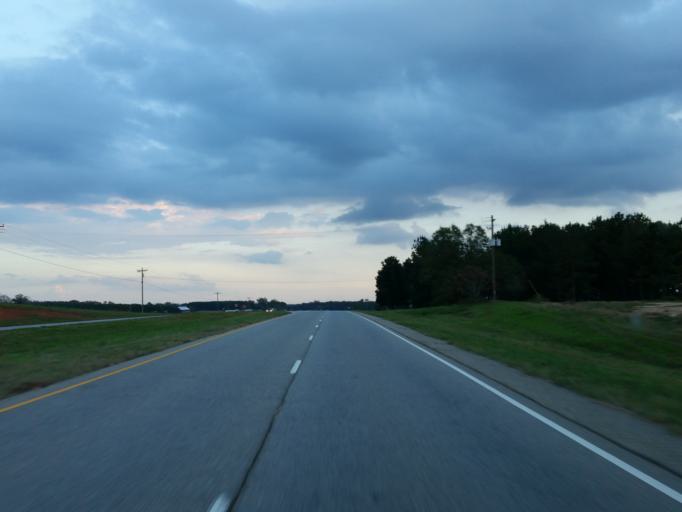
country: US
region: Georgia
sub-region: Pulaski County
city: Hawkinsville
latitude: 32.3204
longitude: -83.5466
